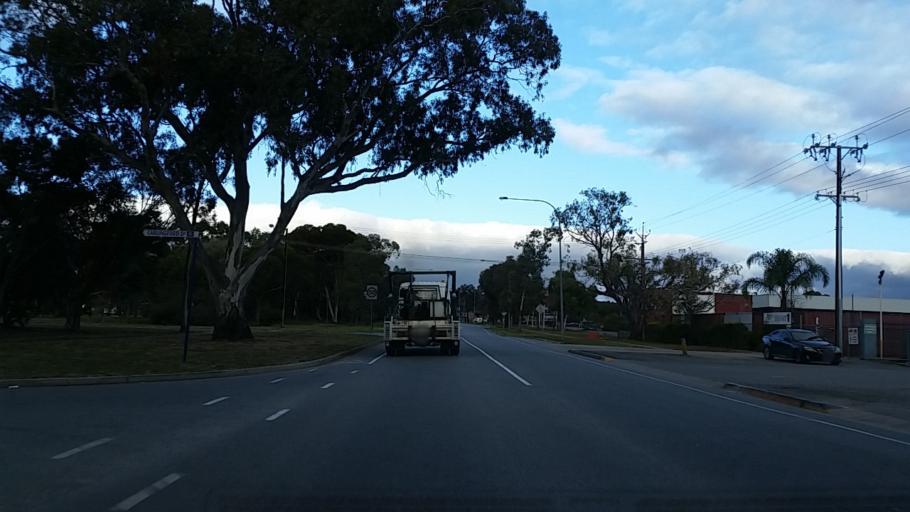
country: AU
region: South Australia
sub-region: Salisbury
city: Salisbury
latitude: -34.7644
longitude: 138.6664
